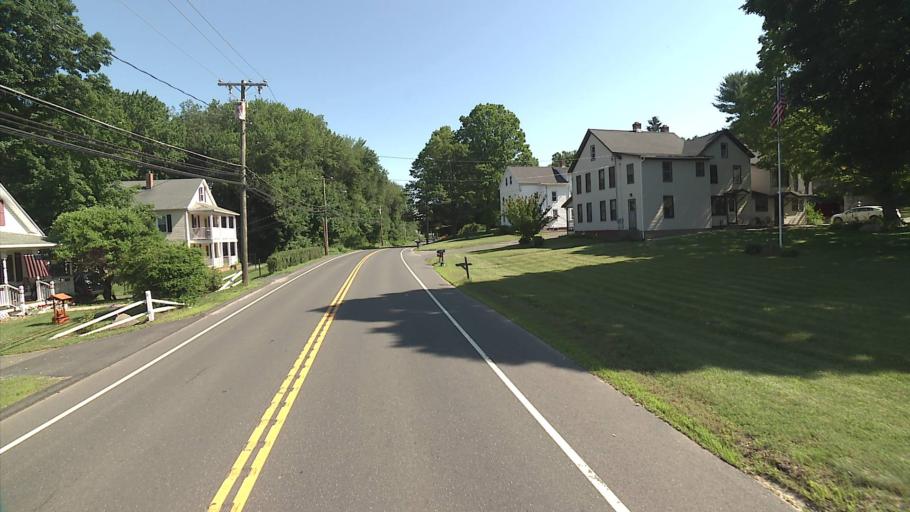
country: US
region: Connecticut
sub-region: Litchfield County
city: Terryville
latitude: 41.6821
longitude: -73.0004
